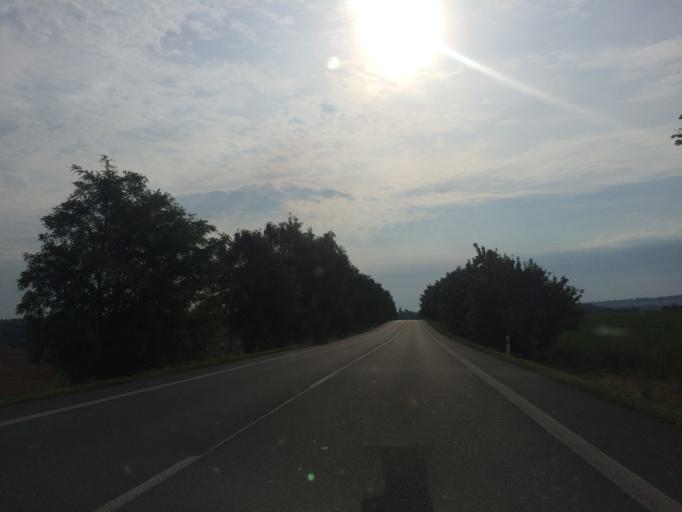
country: CZ
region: Central Bohemia
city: Cesky Brod
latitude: 50.0573
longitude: 14.8978
